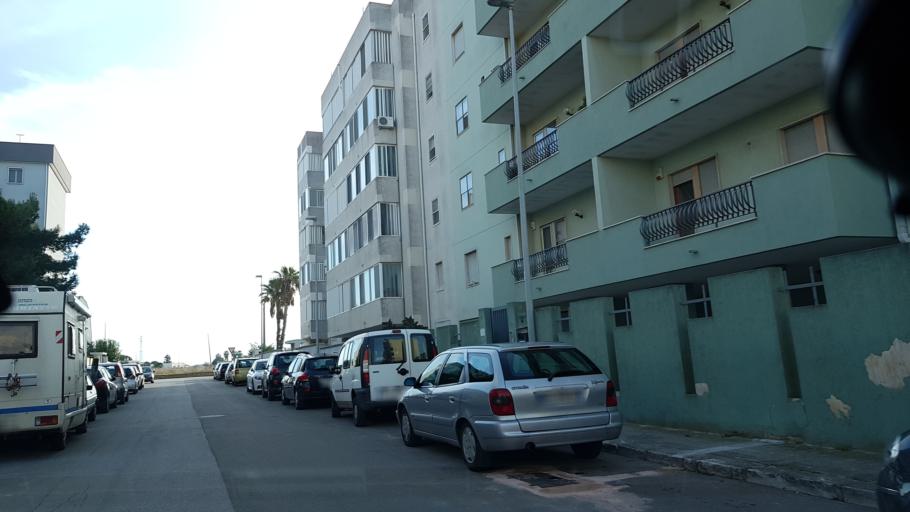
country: IT
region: Apulia
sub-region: Provincia di Brindisi
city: Brindisi
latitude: 40.6178
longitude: 17.9189
